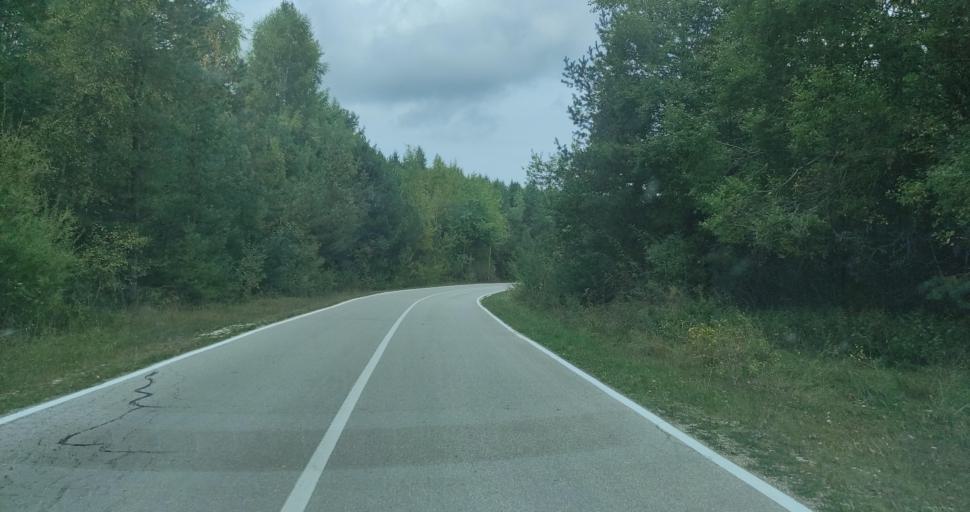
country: RS
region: Central Serbia
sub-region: Jablanicki Okrug
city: Crna Trava
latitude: 42.6984
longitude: 22.3267
